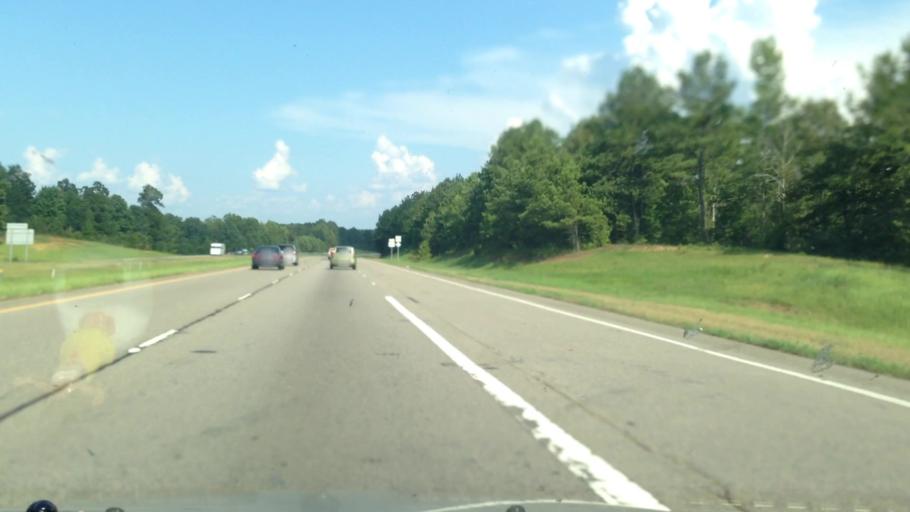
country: US
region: North Carolina
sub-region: Lee County
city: Sanford
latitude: 35.5072
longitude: -79.1638
